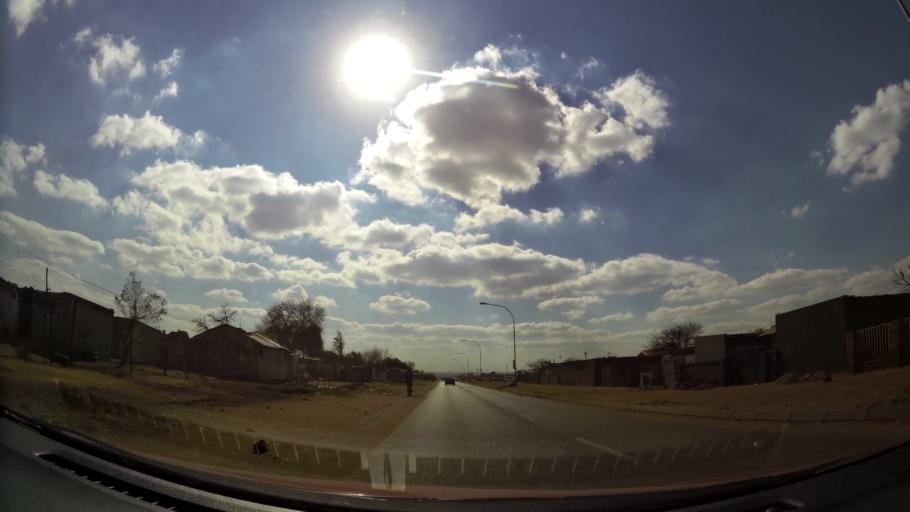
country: ZA
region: Gauteng
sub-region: Ekurhuleni Metropolitan Municipality
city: Tembisa
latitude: -25.9841
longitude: 28.2126
